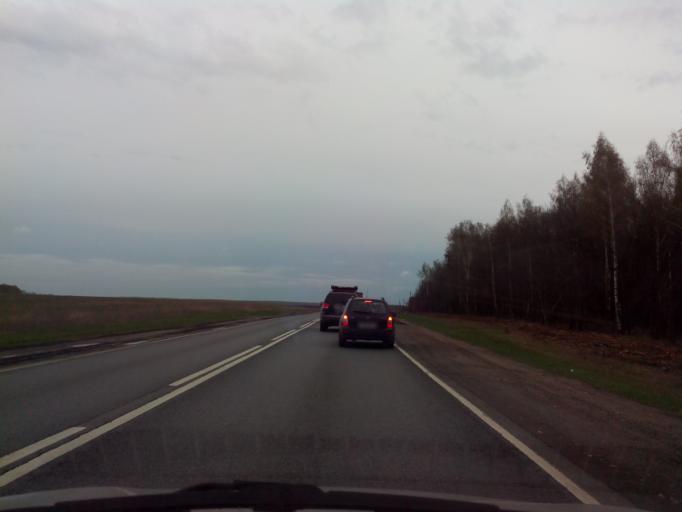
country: RU
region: Moskovskaya
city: Ozherel'ye
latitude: 54.6945
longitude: 38.3137
